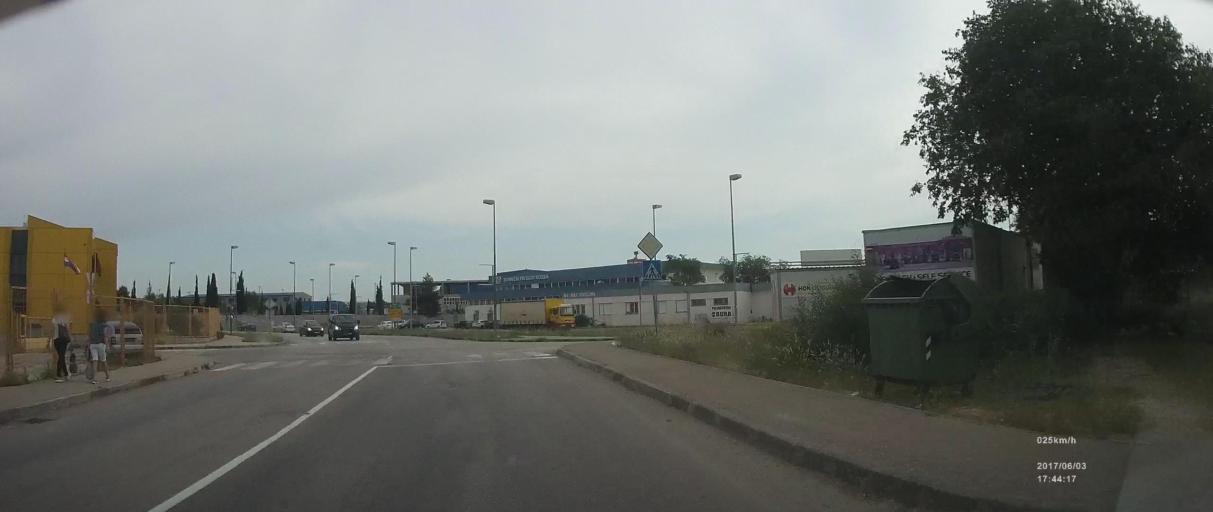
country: HR
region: Sibensko-Kniniska
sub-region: Grad Sibenik
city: Sibenik
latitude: 43.7109
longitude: 15.9102
